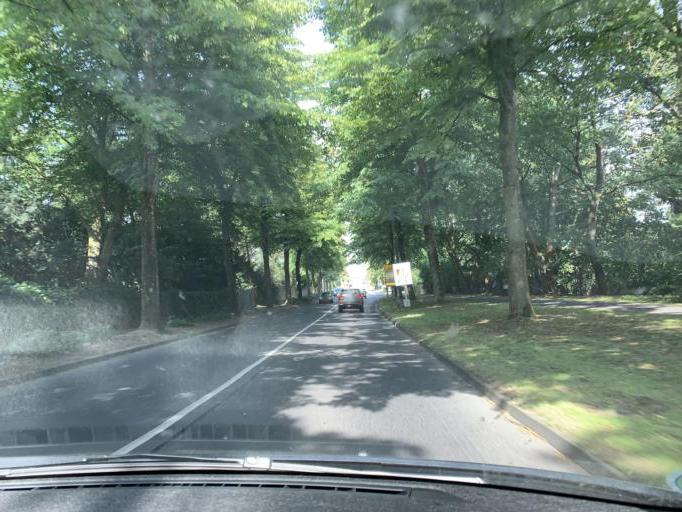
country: DE
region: North Rhine-Westphalia
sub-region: Regierungsbezirk Dusseldorf
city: Viersen
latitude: 51.2606
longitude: 6.3800
